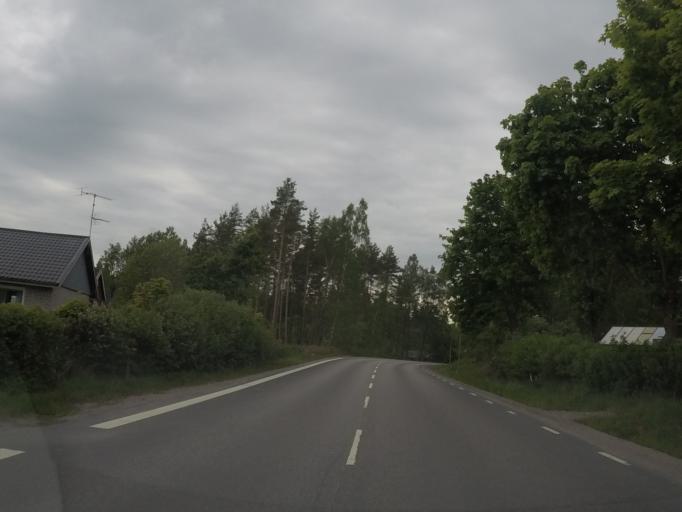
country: SE
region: Soedermanland
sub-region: Eskilstuna Kommun
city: Arla
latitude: 59.2889
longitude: 16.6767
